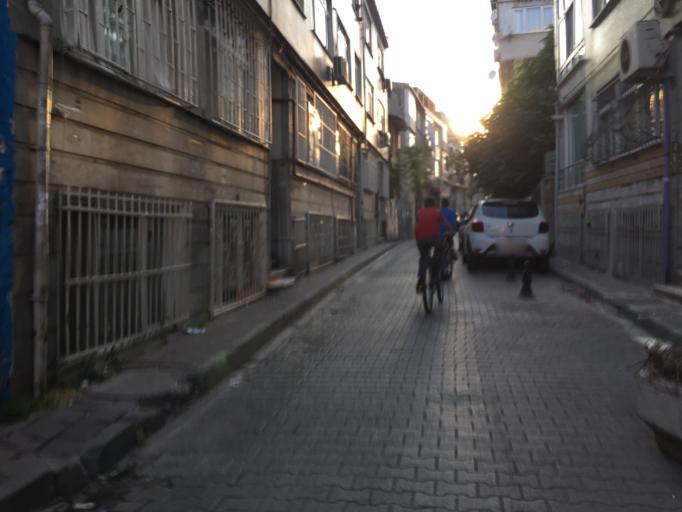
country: TR
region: Istanbul
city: Istanbul
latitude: 41.0222
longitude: 28.9386
